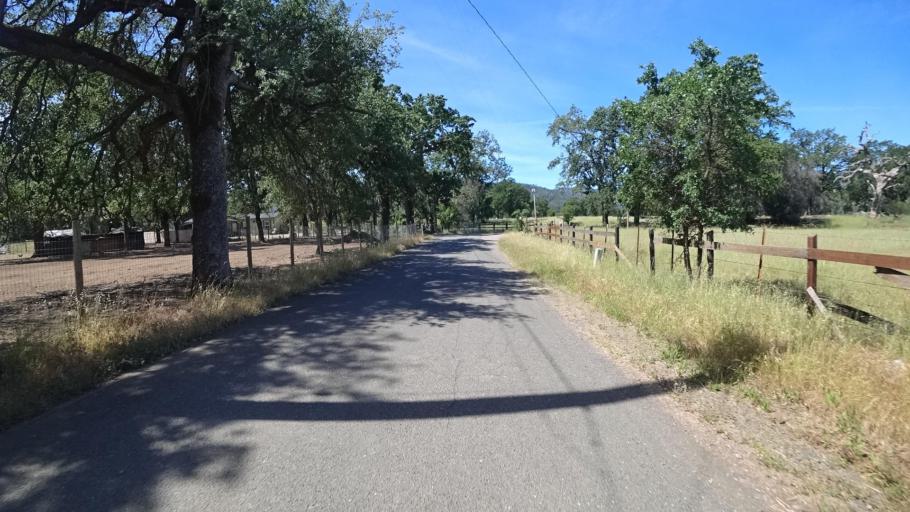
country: US
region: California
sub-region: Lake County
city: Middletown
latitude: 38.7456
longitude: -122.6264
